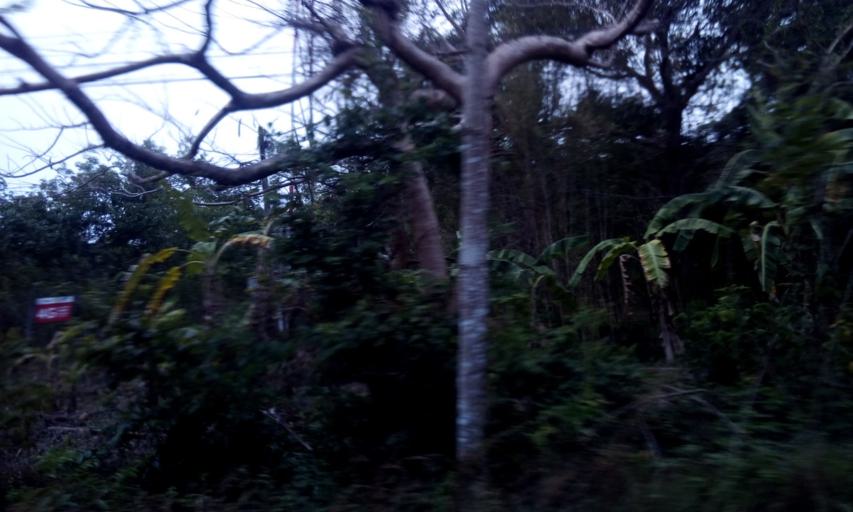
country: TH
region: Trat
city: Laem Ngop
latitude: 12.2671
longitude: 102.3055
